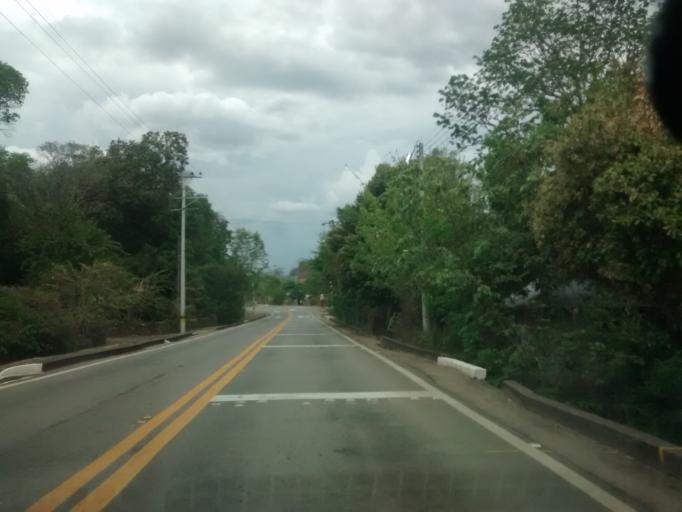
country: CO
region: Cundinamarca
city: Agua de Dios
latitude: 4.4260
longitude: -74.6990
